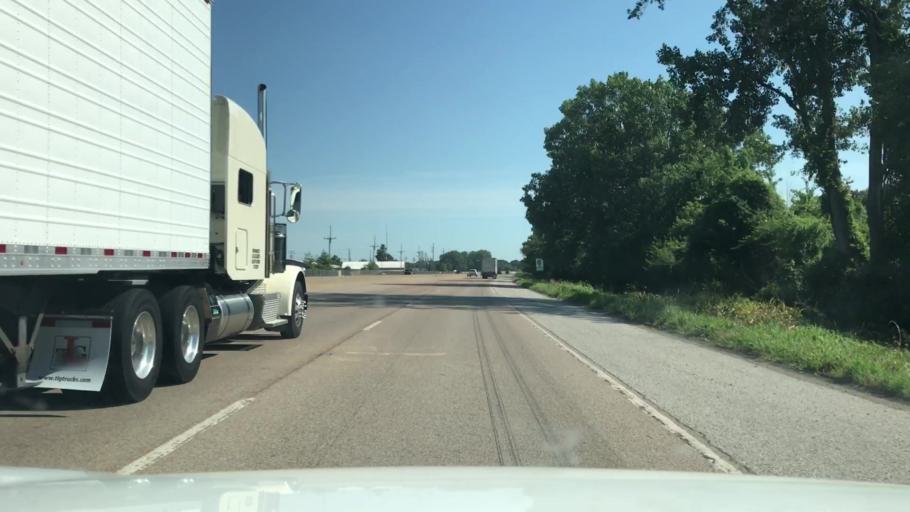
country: US
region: Illinois
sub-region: Madison County
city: Venice
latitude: 38.6868
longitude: -90.1715
